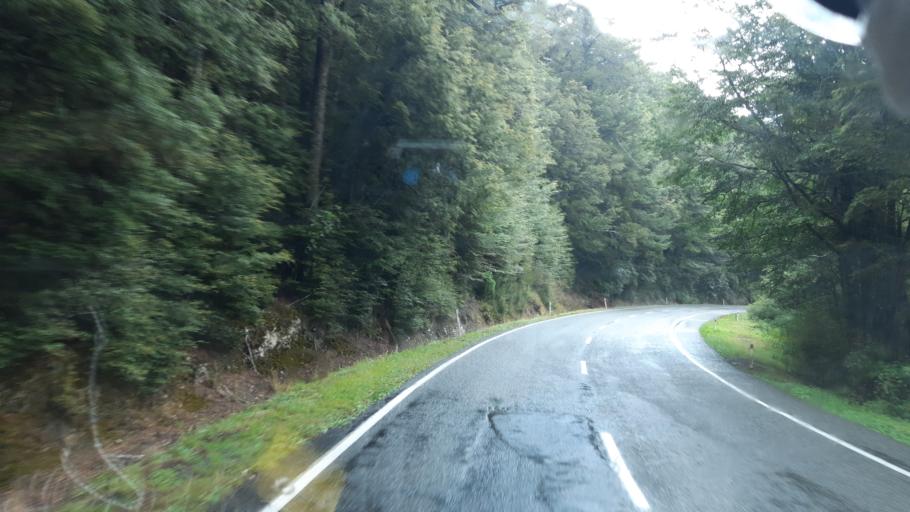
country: NZ
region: Canterbury
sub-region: Hurunui District
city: Amberley
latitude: -42.3786
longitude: 172.3455
